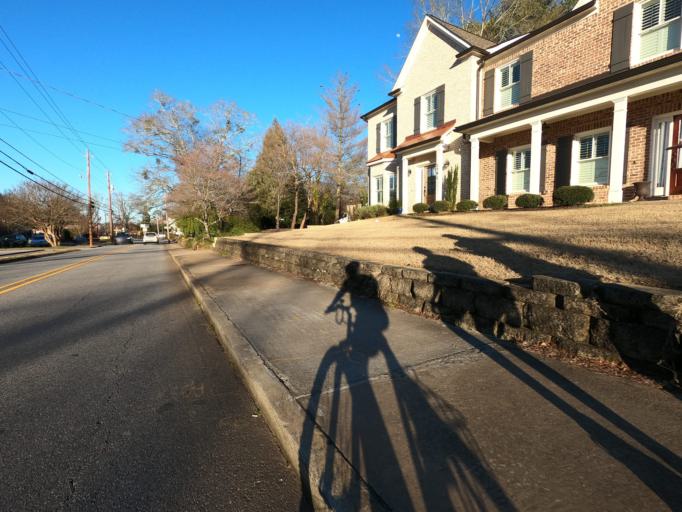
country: US
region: Georgia
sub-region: Clarke County
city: Athens
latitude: 33.9355
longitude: -83.3889
